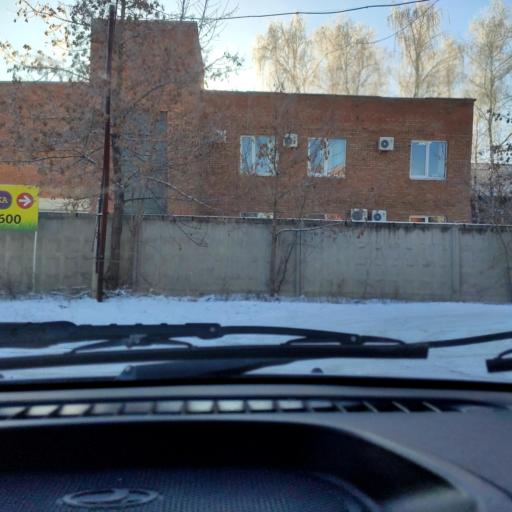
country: RU
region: Samara
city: Zhigulevsk
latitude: 53.4968
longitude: 49.4722
